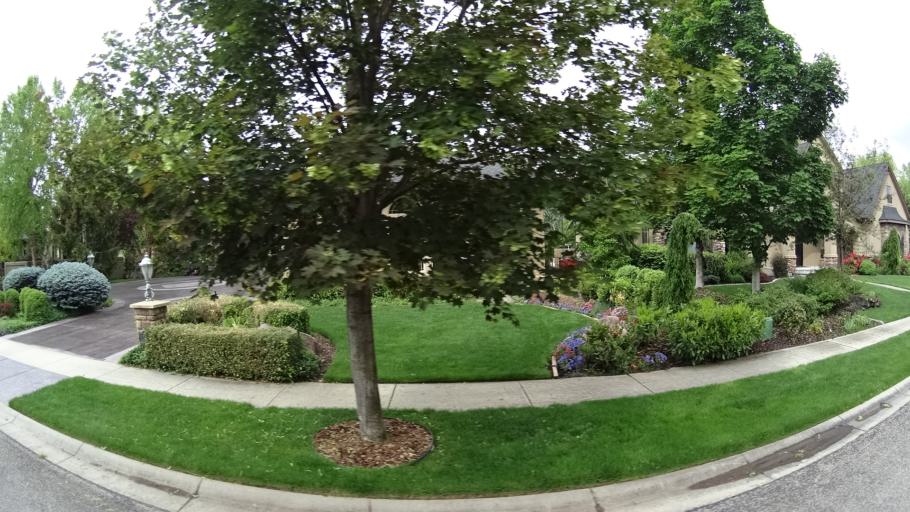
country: US
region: Idaho
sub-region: Ada County
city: Eagle
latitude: 43.6810
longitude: -116.3630
